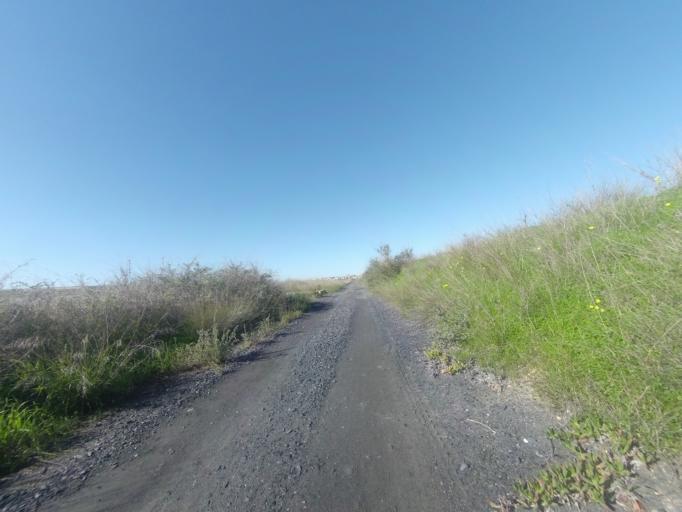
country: ES
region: Andalusia
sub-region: Provincia de Huelva
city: Palos de la Frontera
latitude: 37.2532
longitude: -6.9063
